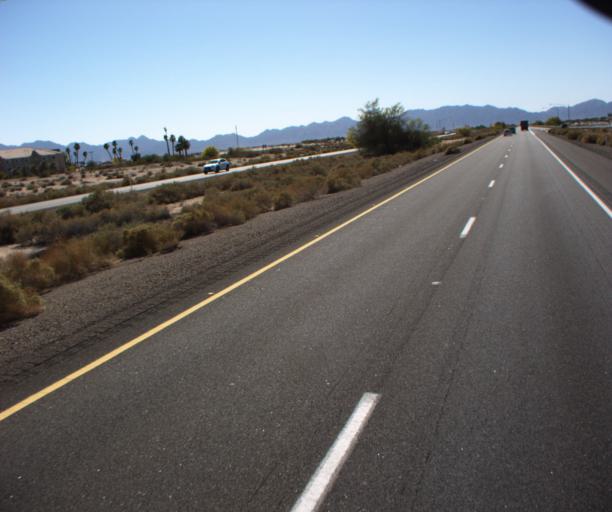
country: US
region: Arizona
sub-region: Yuma County
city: Wellton
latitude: 32.6618
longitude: -114.1432
